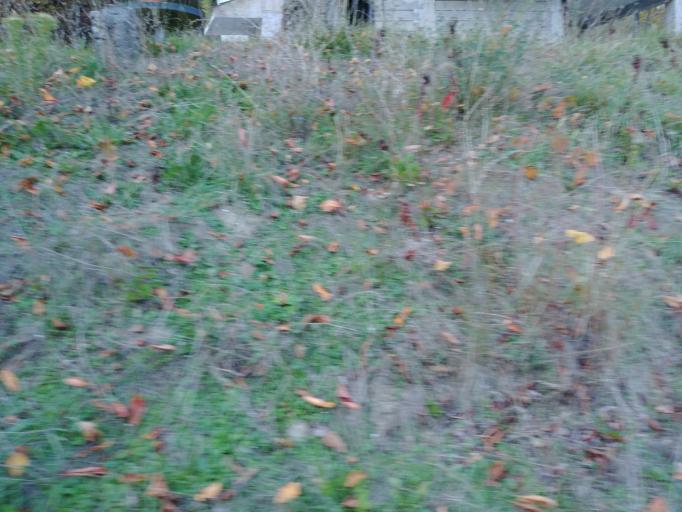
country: IT
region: The Marches
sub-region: Provincia di Ascoli Piceno
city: Arquata del Tronto
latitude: 42.7766
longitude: 13.2919
